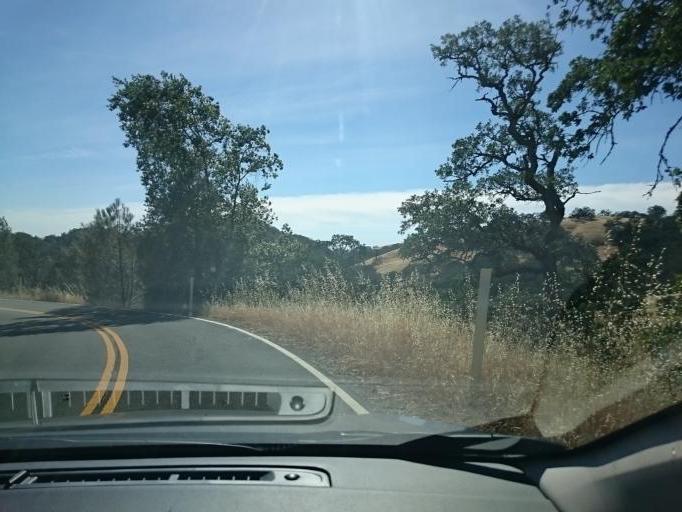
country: US
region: California
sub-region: Santa Clara County
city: East Foothills
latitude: 37.3290
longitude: -121.6661
